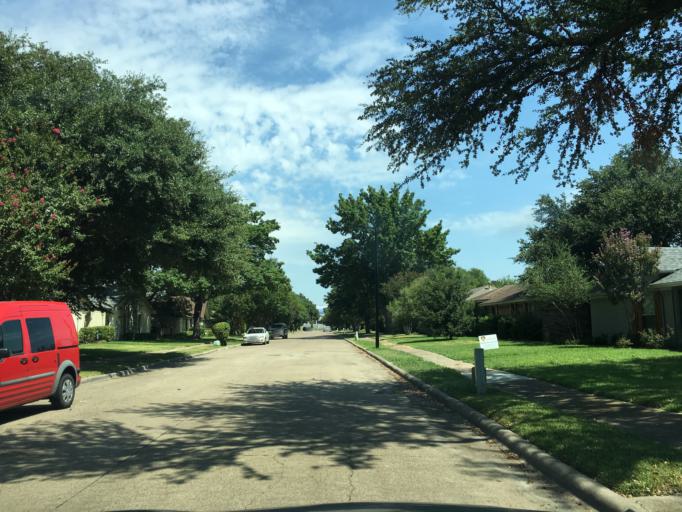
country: US
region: Texas
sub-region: Dallas County
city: Garland
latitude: 32.8669
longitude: -96.6569
